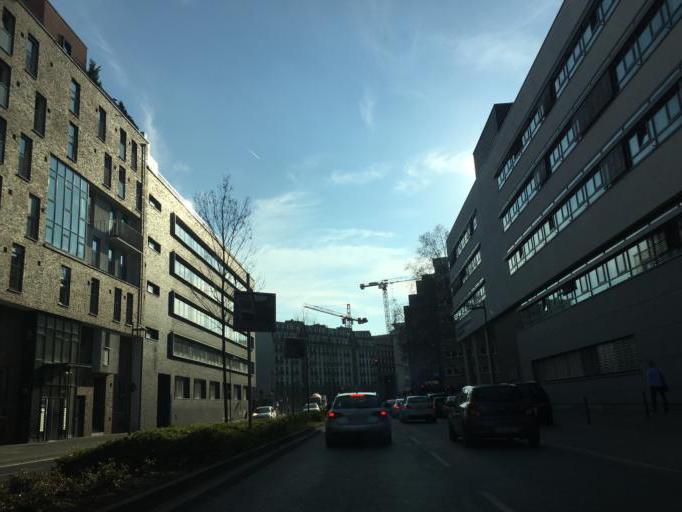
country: DE
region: Hesse
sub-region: Regierungsbezirk Darmstadt
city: Frankfurt am Main
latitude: 50.1098
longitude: 8.6984
